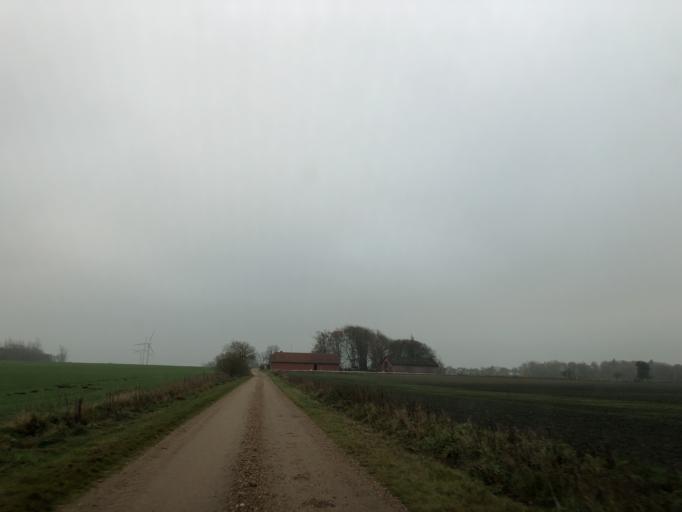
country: DK
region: Central Jutland
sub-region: Herning Kommune
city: Vildbjerg
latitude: 56.2093
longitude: 8.7254
